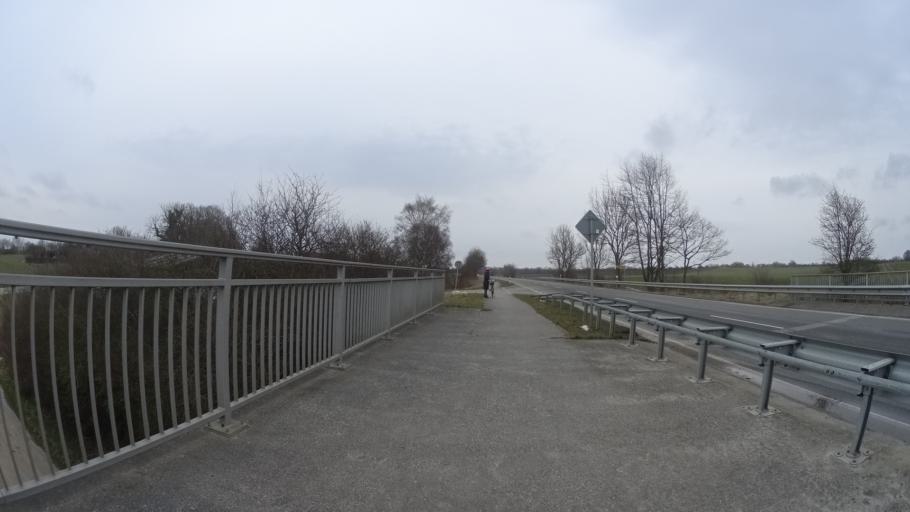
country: DE
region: Schleswig-Holstein
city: Stakendorf
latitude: 54.3771
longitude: 10.4599
